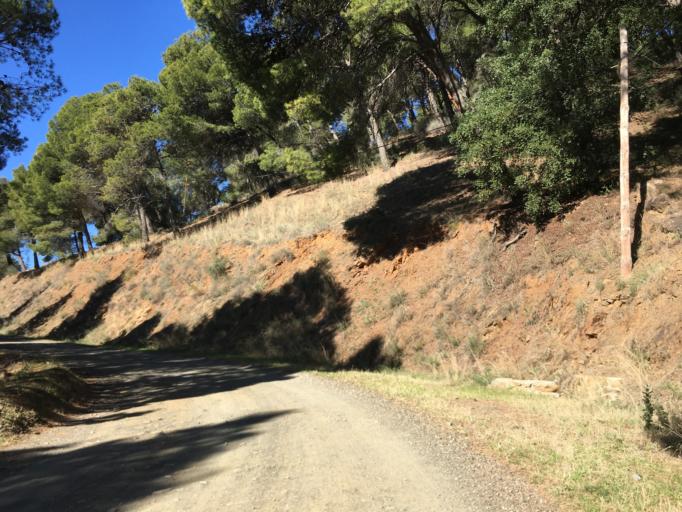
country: ES
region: Andalusia
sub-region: Provincia de Malaga
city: Malaga
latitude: 36.7826
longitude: -4.3892
